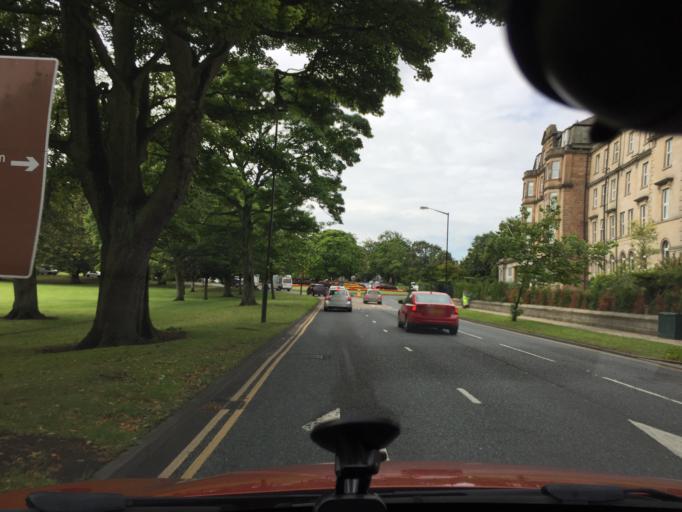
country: GB
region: England
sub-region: North Yorkshire
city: Harrogate
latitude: 53.9877
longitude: -1.5377
